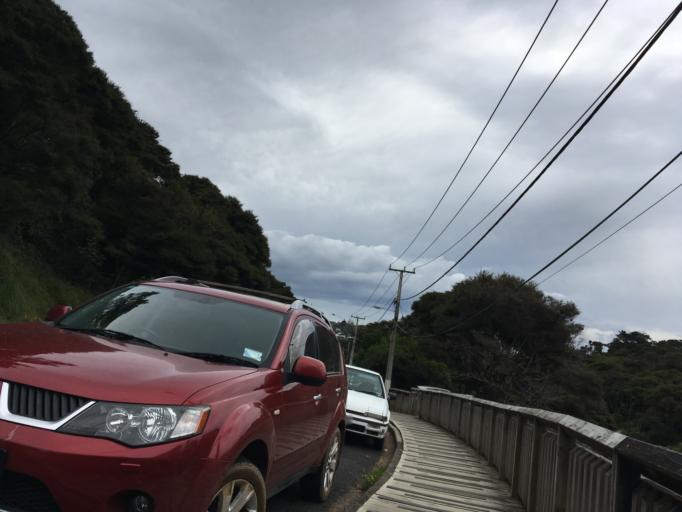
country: NZ
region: Auckland
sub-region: Auckland
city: Pakuranga
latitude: -36.7866
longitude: 175.0215
